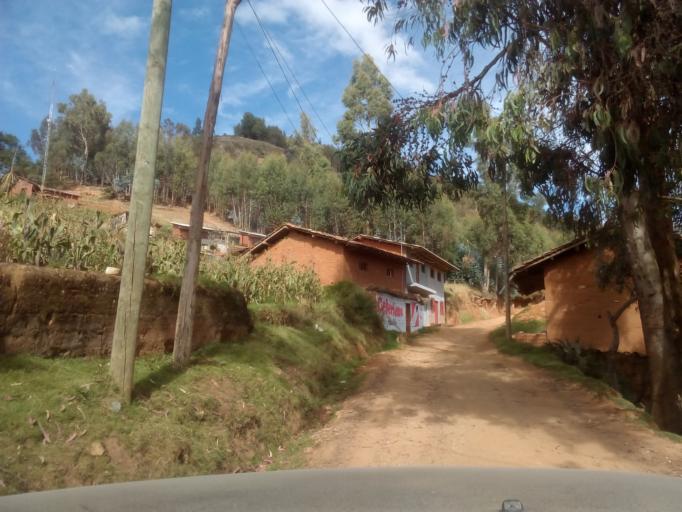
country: PE
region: La Libertad
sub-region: Sanchez Carrion
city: Curgos
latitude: -7.8644
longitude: -77.9404
